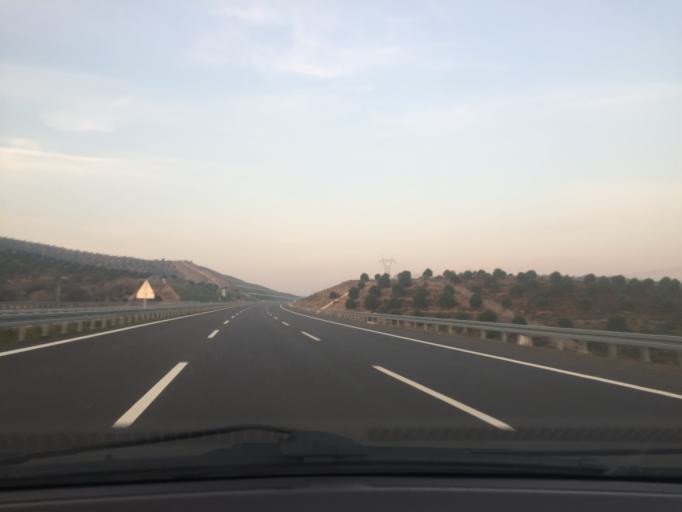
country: TR
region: Bursa
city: Mahmudiye
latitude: 40.2742
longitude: 28.5629
